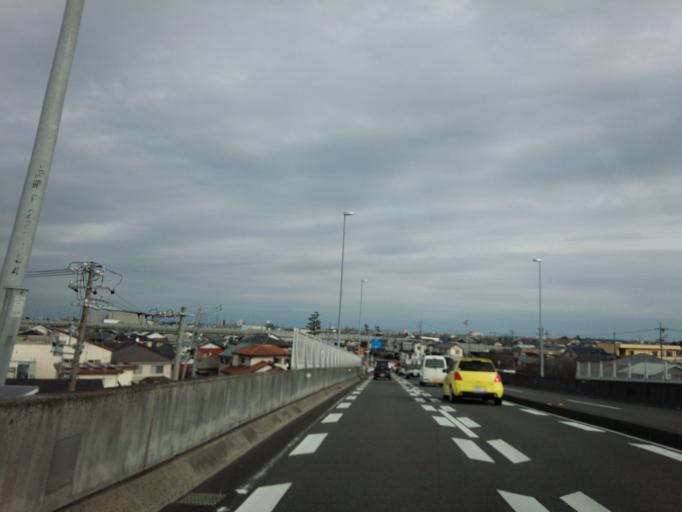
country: JP
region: Shizuoka
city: Yaizu
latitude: 34.8636
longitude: 138.2978
